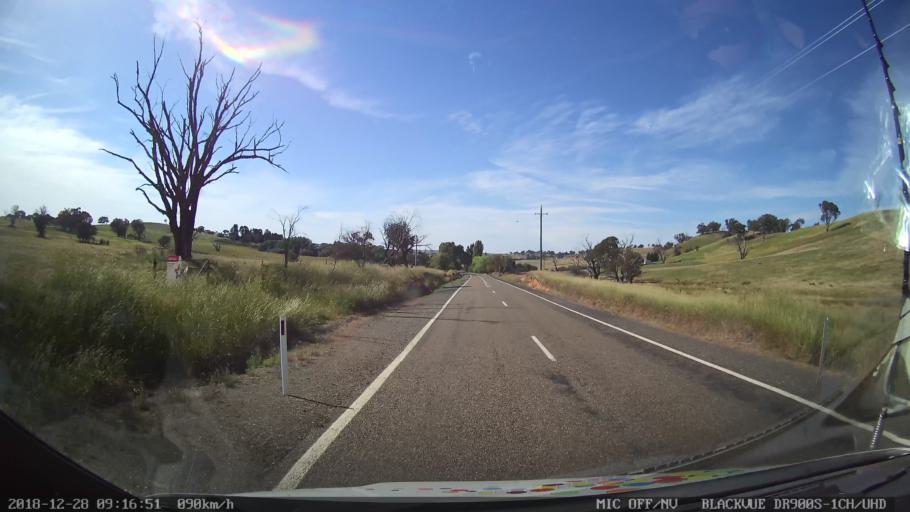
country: AU
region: New South Wales
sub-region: Upper Lachlan Shire
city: Crookwell
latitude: -34.3140
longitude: 149.3574
